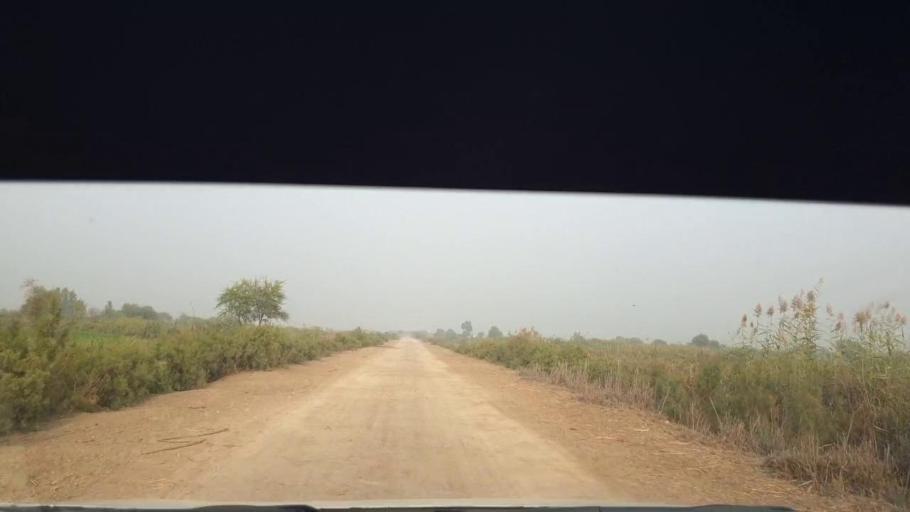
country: PK
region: Sindh
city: Berani
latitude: 25.8144
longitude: 68.8832
